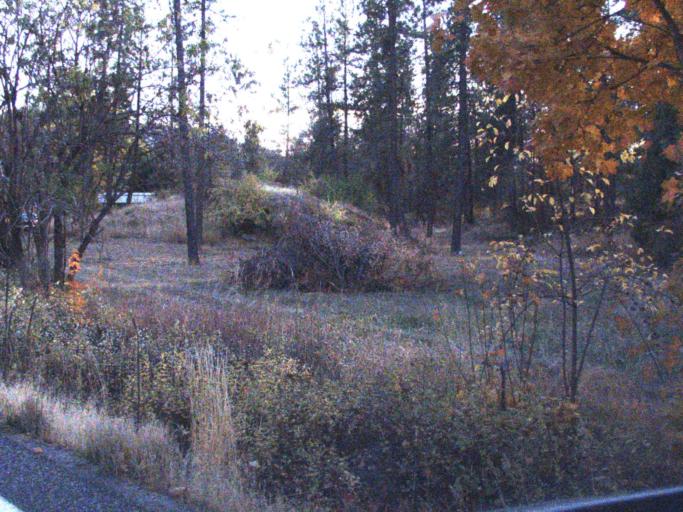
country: US
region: Washington
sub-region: Stevens County
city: Kettle Falls
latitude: 48.7115
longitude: -118.0225
